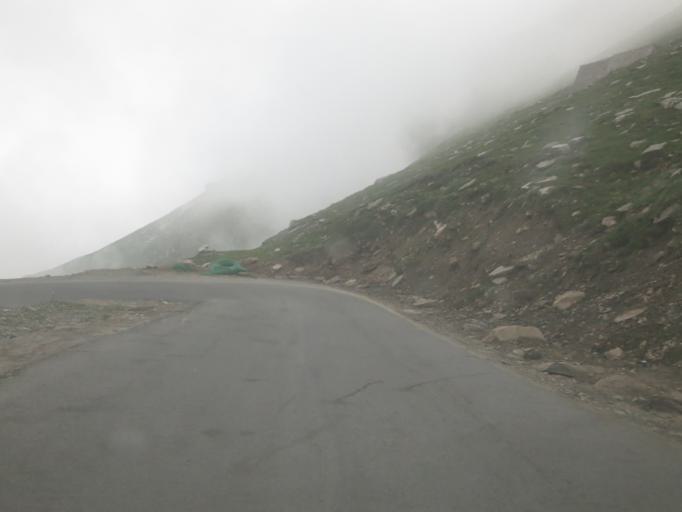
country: IN
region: Himachal Pradesh
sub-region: Kulu
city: Manali
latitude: 32.3639
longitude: 77.2392
